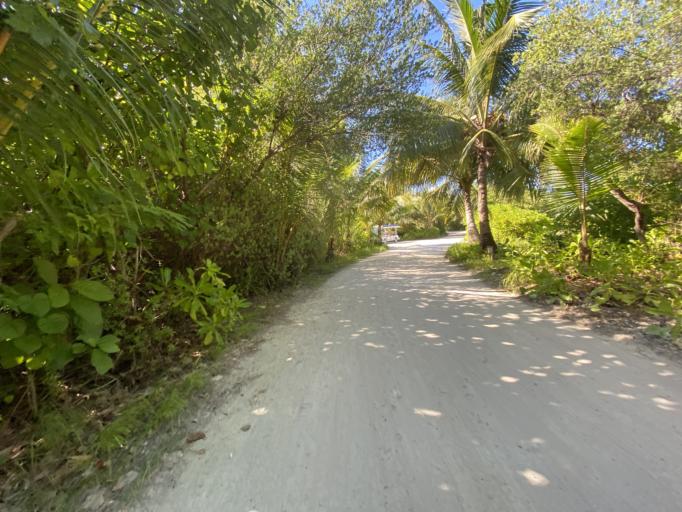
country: MV
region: Seenu
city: Meedhoo
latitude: -0.6281
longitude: 73.2257
